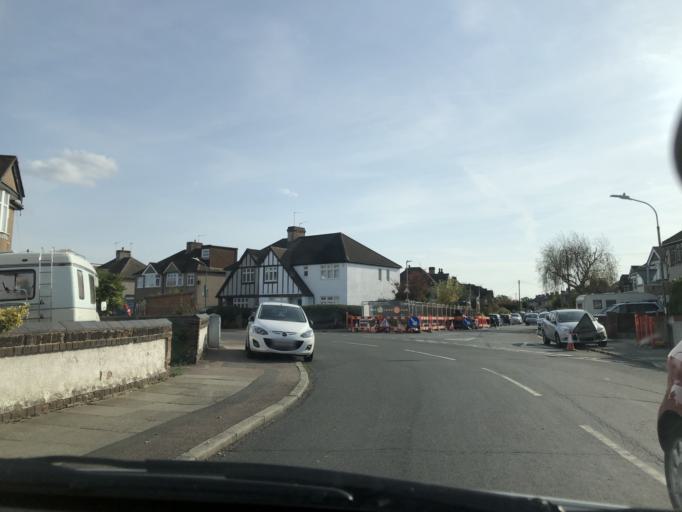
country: GB
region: England
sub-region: Kent
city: Dartford
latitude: 51.4431
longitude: 0.1868
